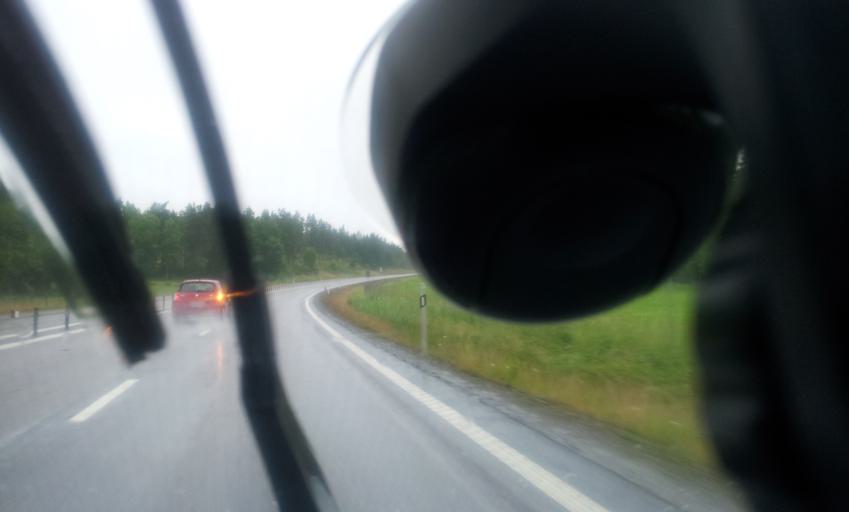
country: SE
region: OEstergoetland
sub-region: Soderkopings Kommun
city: Soederkoeping
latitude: 58.4276
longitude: 16.3853
